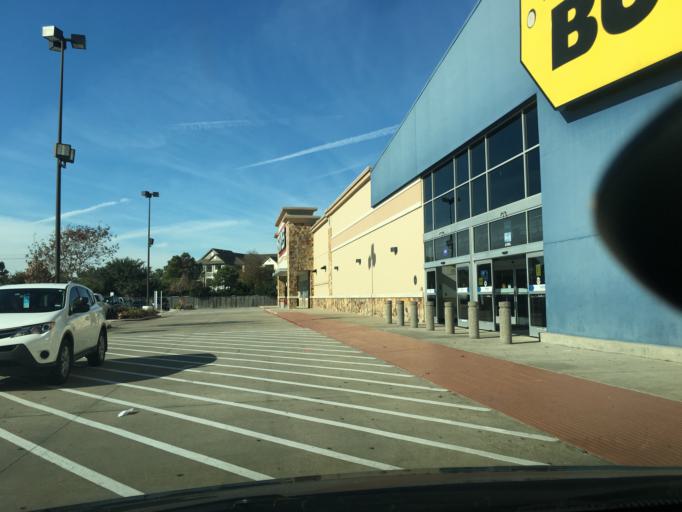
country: US
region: Texas
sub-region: Harris County
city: Cloverleaf
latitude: 29.8117
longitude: -95.1621
